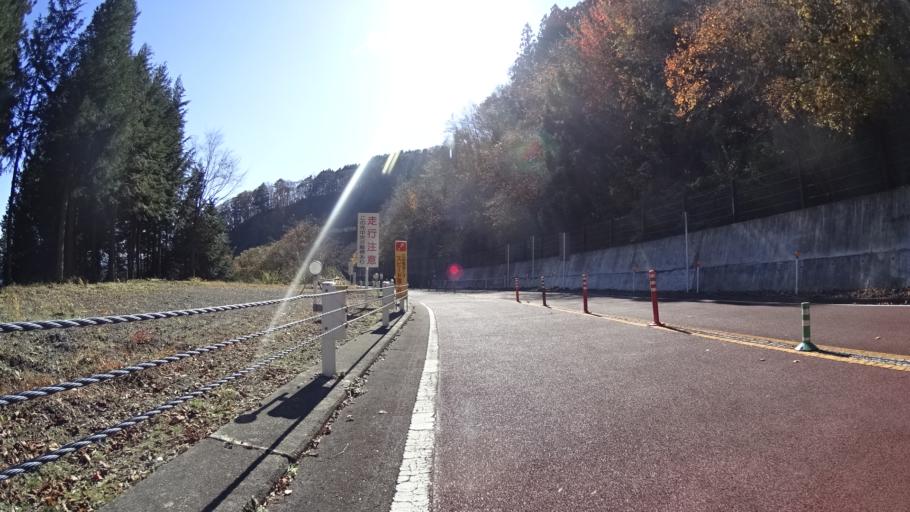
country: JP
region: Yamanashi
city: Uenohara
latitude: 35.7459
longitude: 139.0424
